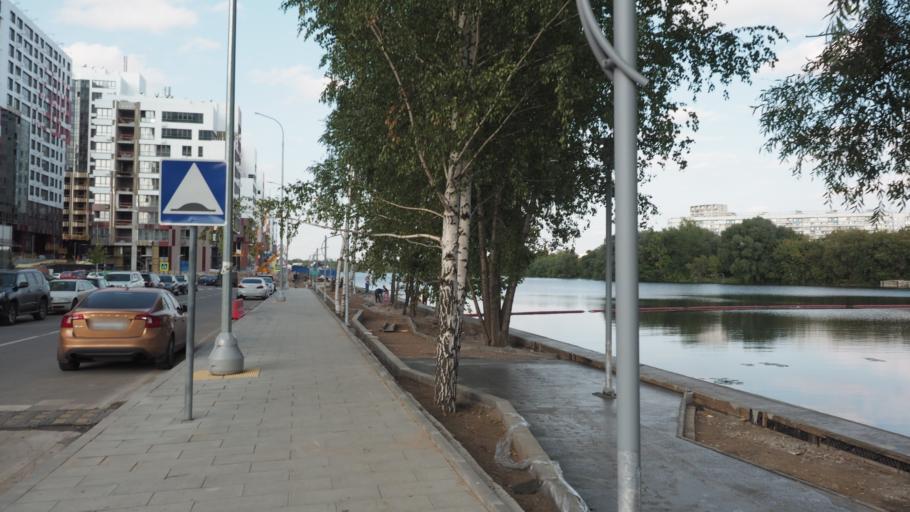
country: RU
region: Moscow
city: Kolomenskoye
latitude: 55.6802
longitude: 37.6965
